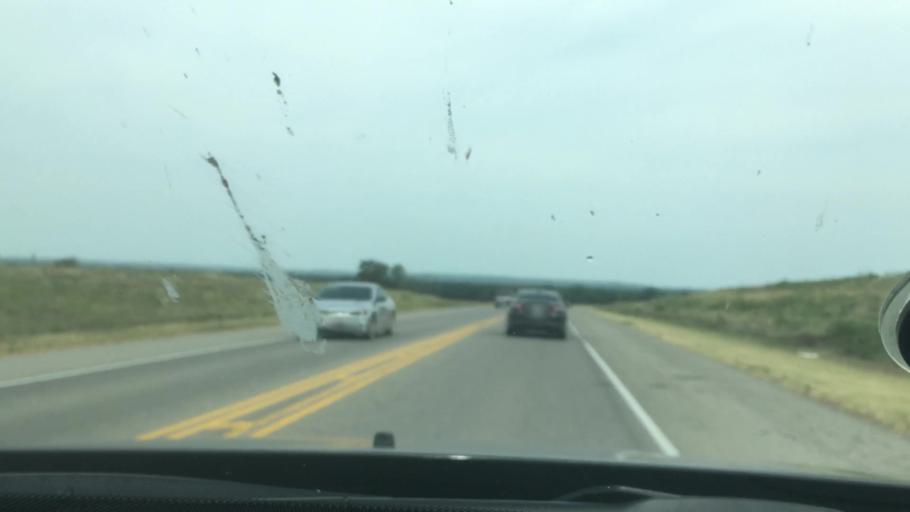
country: US
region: Oklahoma
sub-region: Pontotoc County
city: Ada
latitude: 34.6815
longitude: -96.5850
